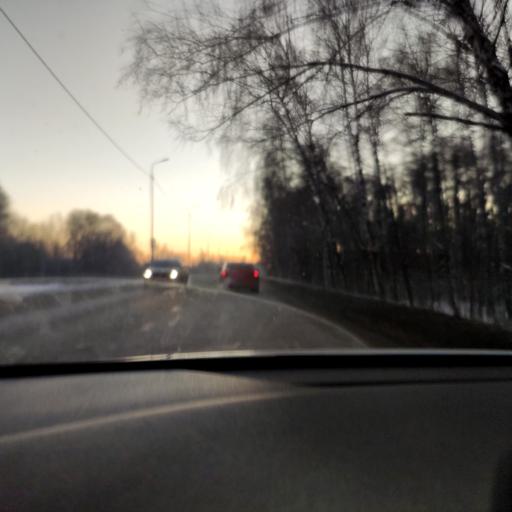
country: RU
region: Tatarstan
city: Osinovo
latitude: 55.8639
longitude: 48.9337
